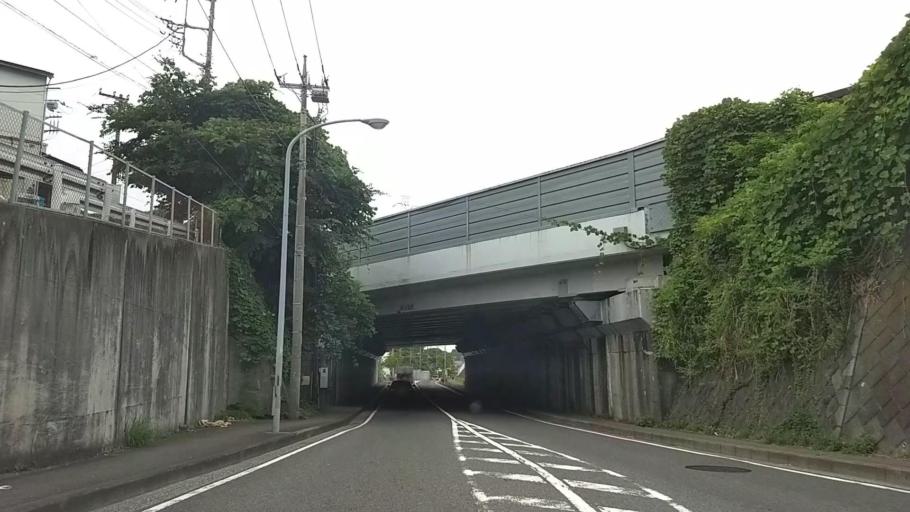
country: JP
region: Kanagawa
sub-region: Kawasaki-shi
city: Kawasaki
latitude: 35.5608
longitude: 139.6097
